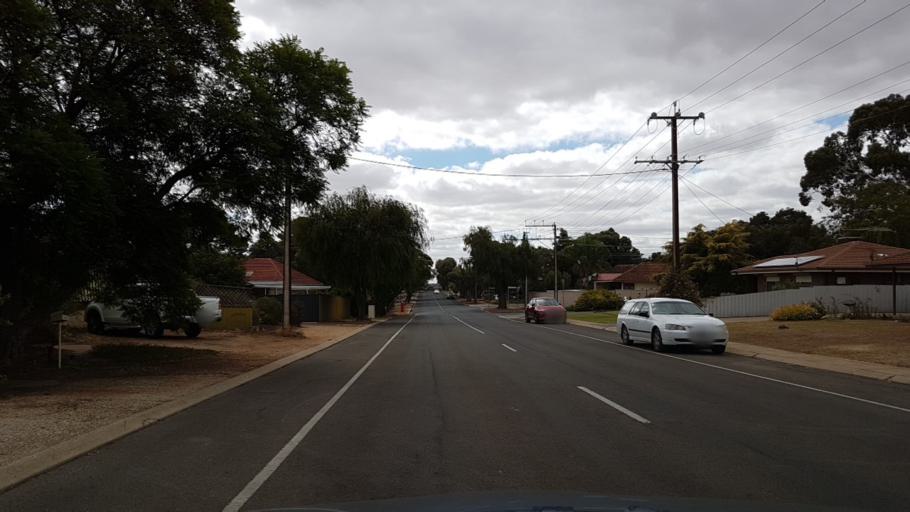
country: AU
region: South Australia
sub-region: Gawler
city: Gawler
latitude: -34.6053
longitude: 138.7570
